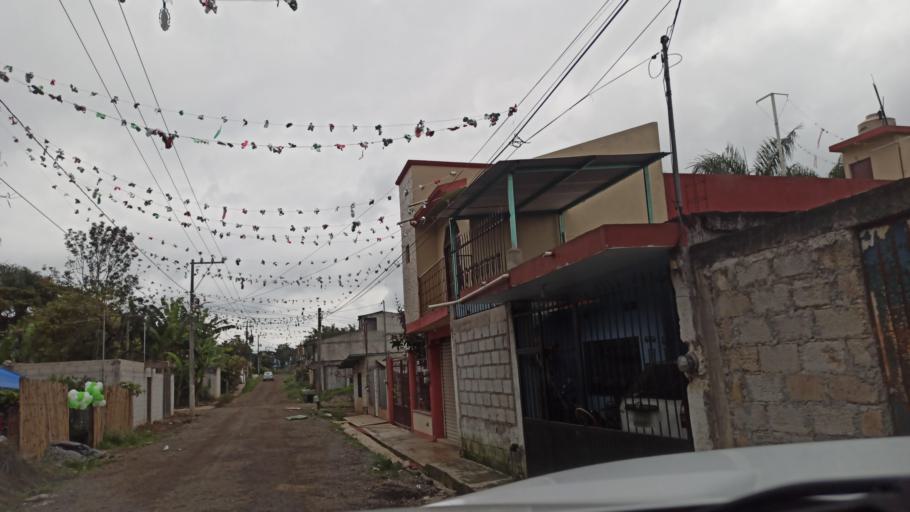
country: MX
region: Veracruz
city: Monte Blanco
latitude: 18.9677
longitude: -97.0157
